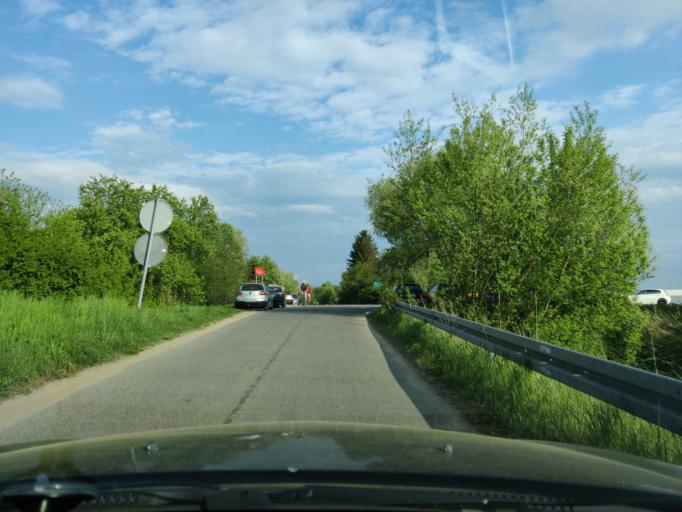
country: PL
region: Masovian Voivodeship
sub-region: Powiat otwocki
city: Jozefow
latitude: 52.1102
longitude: 21.1863
